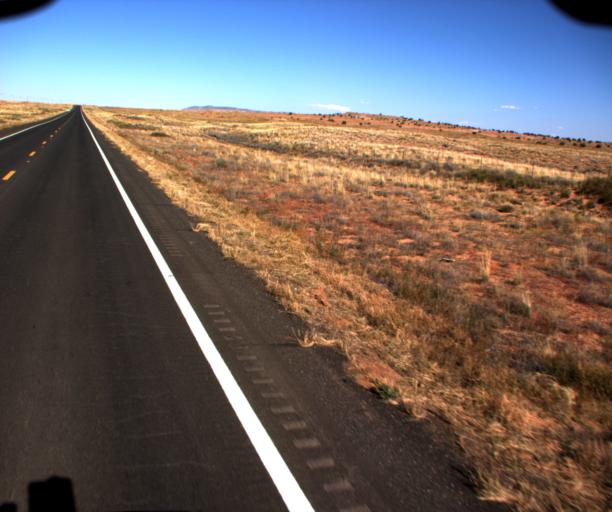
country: US
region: Arizona
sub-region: Coconino County
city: Tuba City
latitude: 36.2843
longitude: -110.9992
